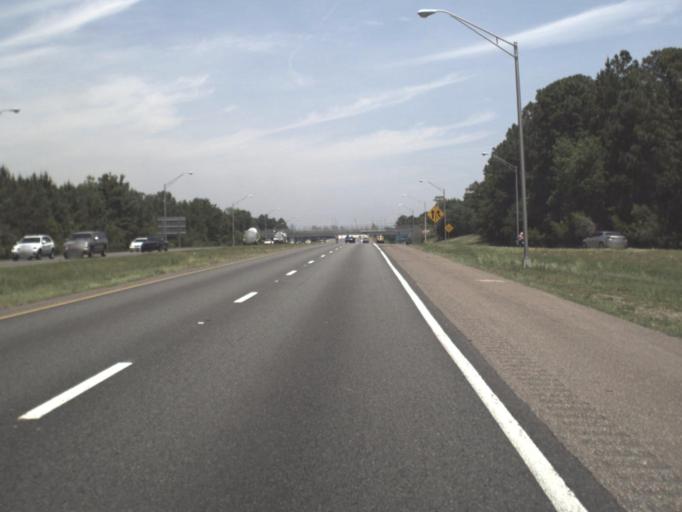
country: US
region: Florida
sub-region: Duval County
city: Jacksonville
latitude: 30.3579
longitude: -81.5545
